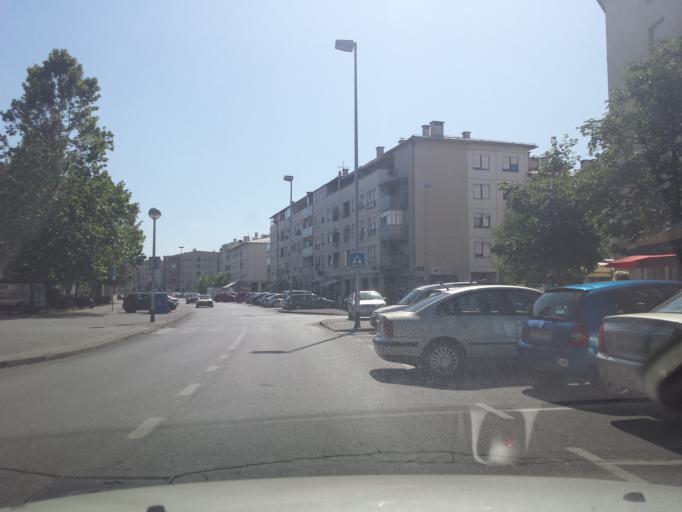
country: HR
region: Grad Zagreb
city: Jankomir
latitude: 45.7931
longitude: 15.9158
